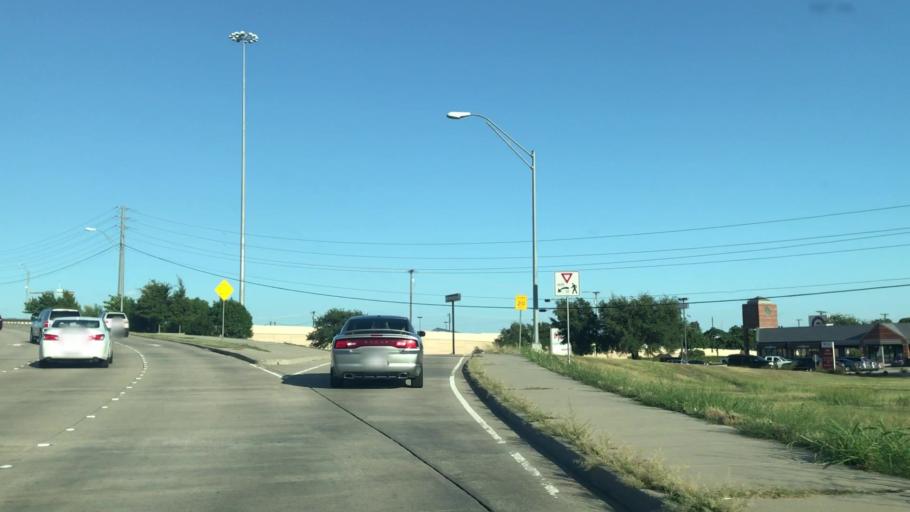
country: US
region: Texas
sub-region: Collin County
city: Plano
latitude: 33.0378
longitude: -96.7066
